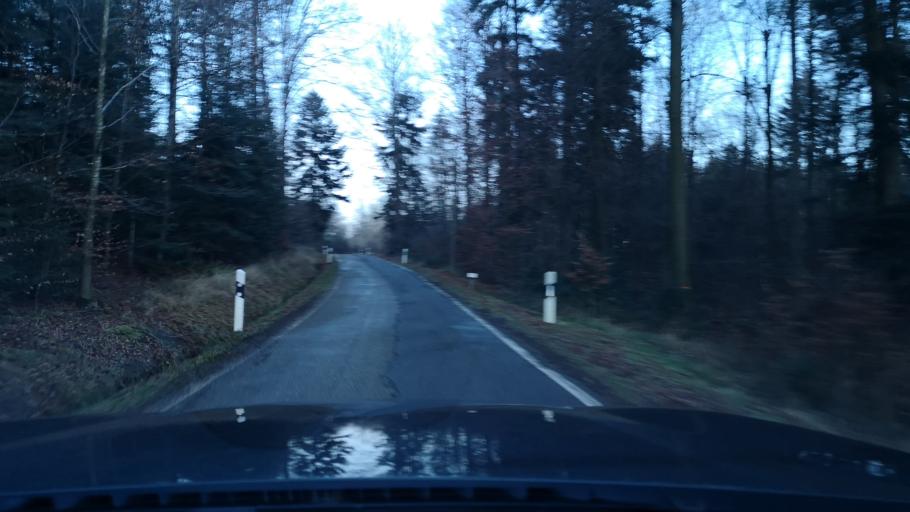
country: DE
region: Baden-Wuerttemberg
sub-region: Regierungsbezirk Stuttgart
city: Kaisersbach
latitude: 48.9429
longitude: 9.6753
